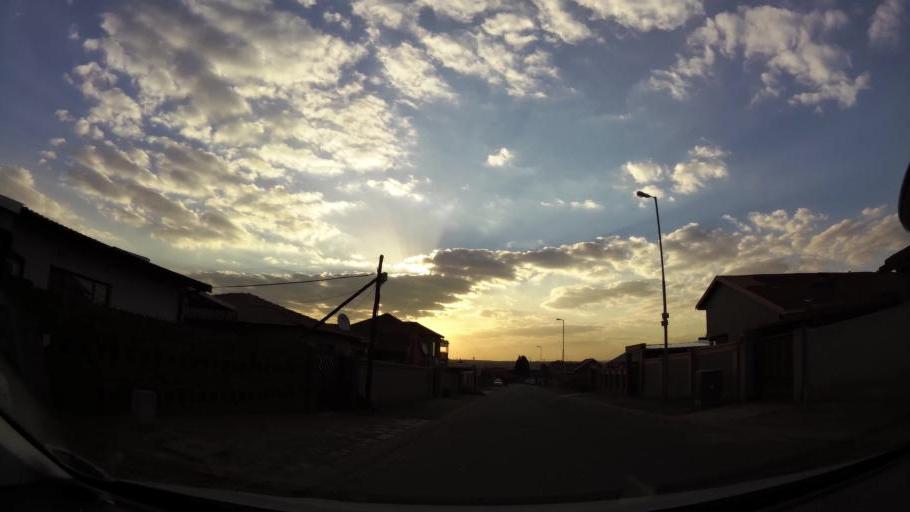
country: ZA
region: Gauteng
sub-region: City of Johannesburg Metropolitan Municipality
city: Soweto
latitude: -26.2698
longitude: 27.8952
